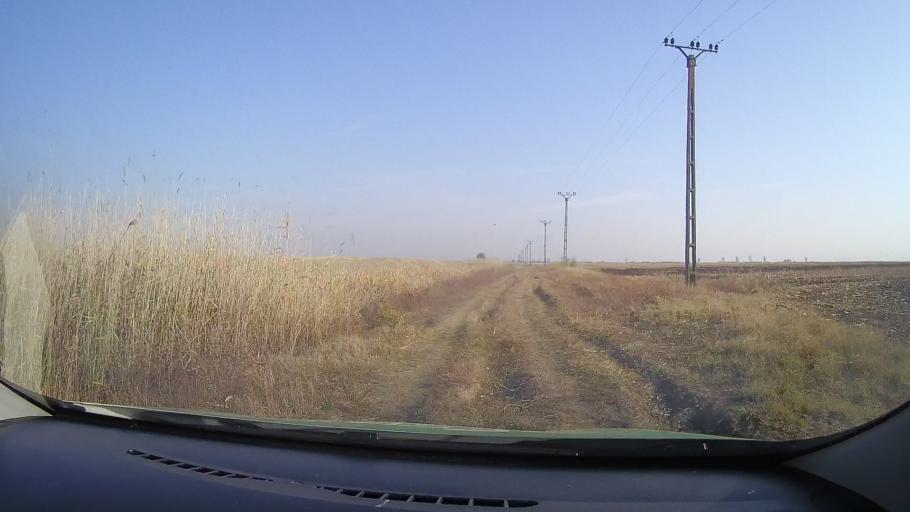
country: RO
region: Arad
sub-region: Comuna Pilu
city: Pilu
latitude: 46.5468
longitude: 21.3312
